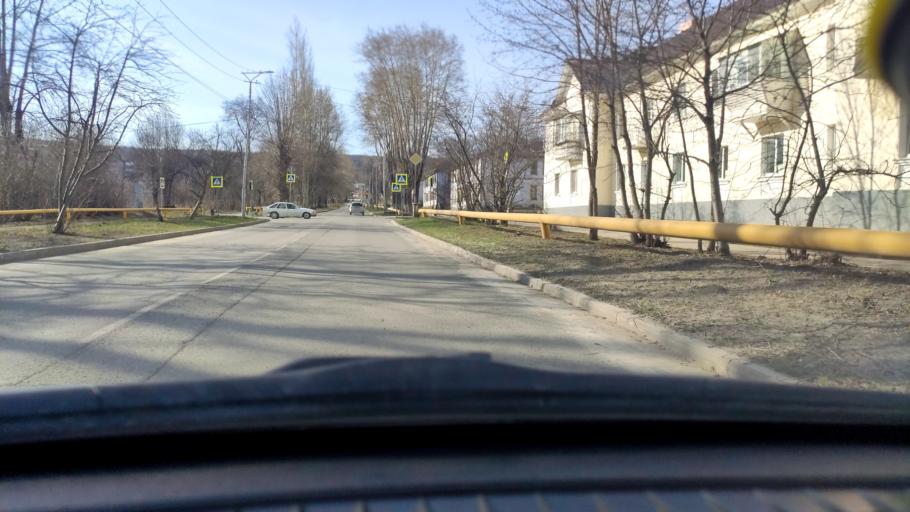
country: RU
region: Samara
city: Zhigulevsk
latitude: 53.3999
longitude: 49.4976
